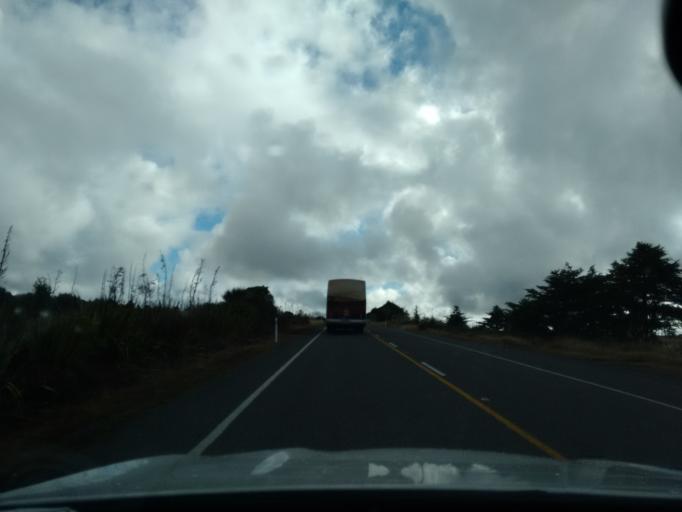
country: NZ
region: Manawatu-Wanganui
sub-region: Ruapehu District
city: Waiouru
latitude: -39.1787
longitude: 175.4620
